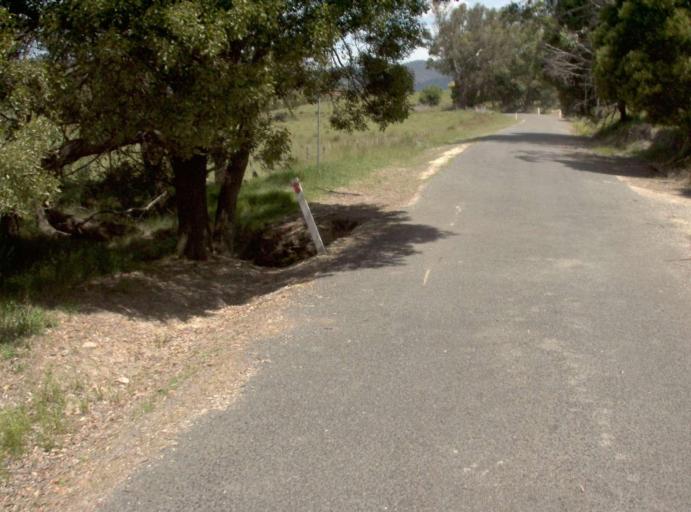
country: AU
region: New South Wales
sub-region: Bombala
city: Bombala
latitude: -37.3877
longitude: 149.0129
